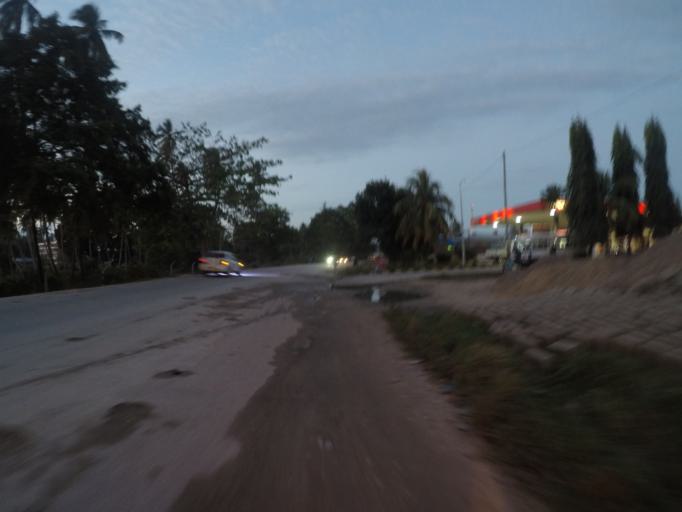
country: TZ
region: Zanzibar Urban/West
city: Zanzibar
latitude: -6.0920
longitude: 39.2197
